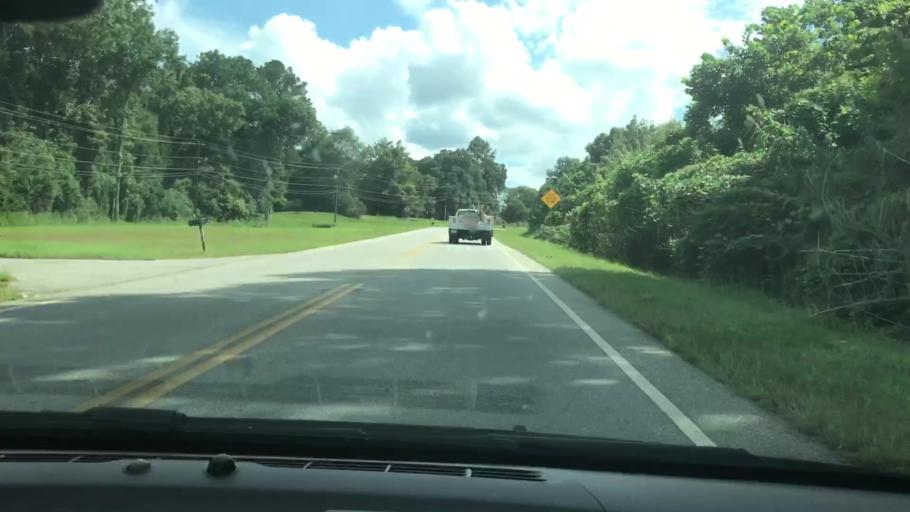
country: US
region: Georgia
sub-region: Clay County
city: Fort Gaines
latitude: 31.6233
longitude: -85.0459
